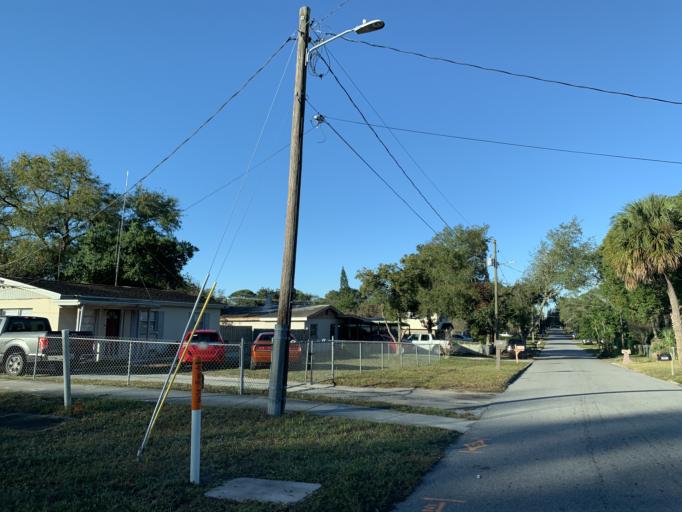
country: US
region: Florida
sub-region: Hillsborough County
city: University
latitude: 28.0391
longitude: -82.4264
